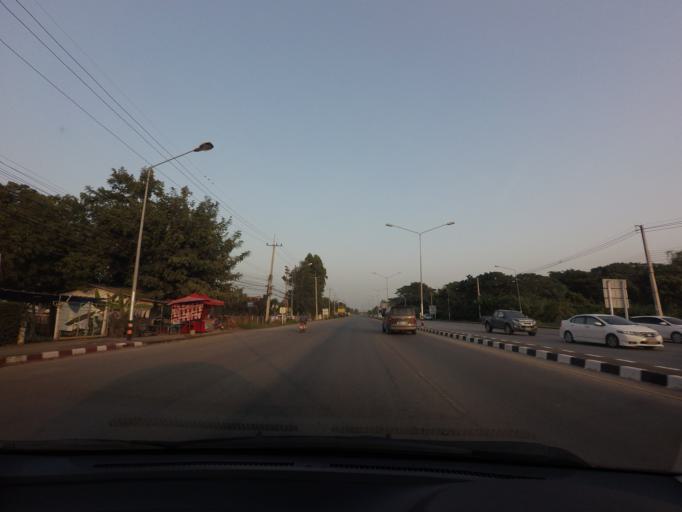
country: TH
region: Sukhothai
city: Sukhothai
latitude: 17.0263
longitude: 99.8826
